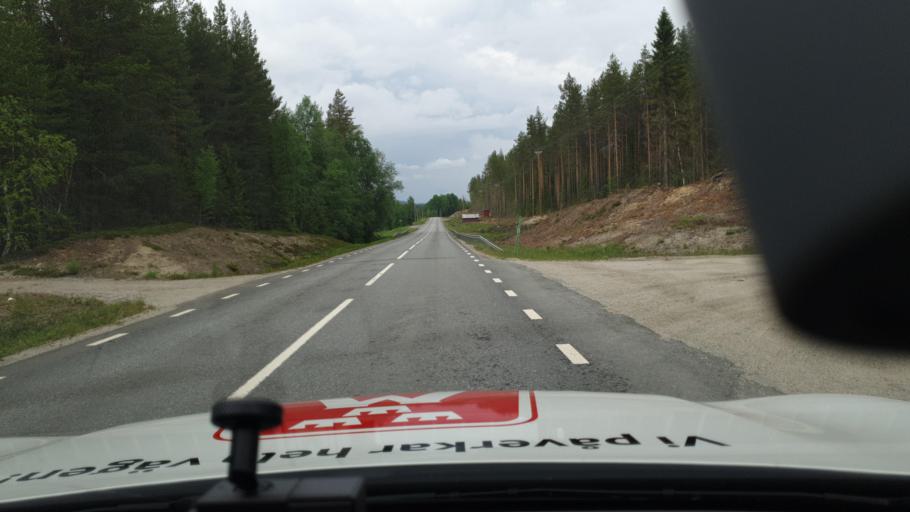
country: SE
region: Vaesterbotten
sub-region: Bjurholms Kommun
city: Bjurholm
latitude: 64.3487
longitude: 19.1488
